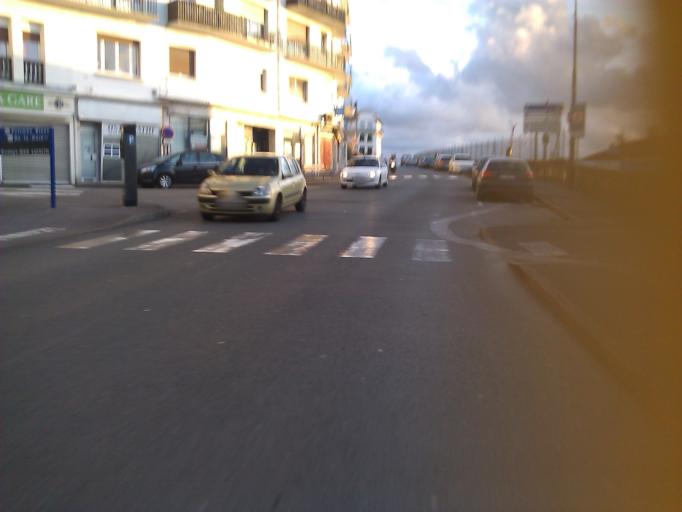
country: ES
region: Basque Country
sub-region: Provincia de Guipuzcoa
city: Irun
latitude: 43.3526
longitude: -1.7816
